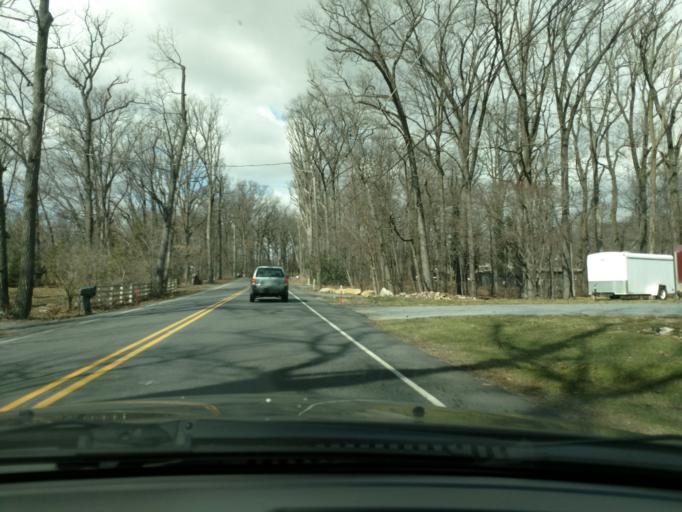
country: US
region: Pennsylvania
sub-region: Lebanon County
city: Myerstown
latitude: 40.4005
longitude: -76.3033
